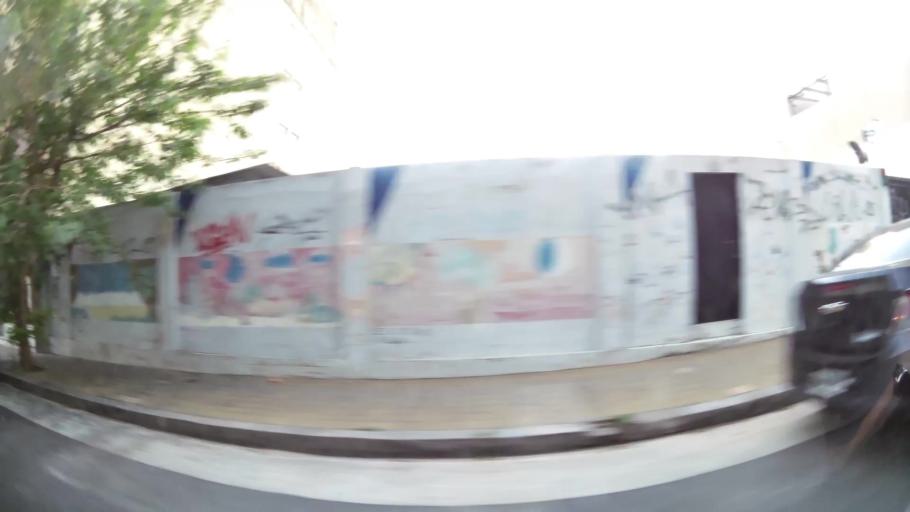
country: AR
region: Buenos Aires F.D.
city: Colegiales
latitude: -34.5465
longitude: -58.4756
